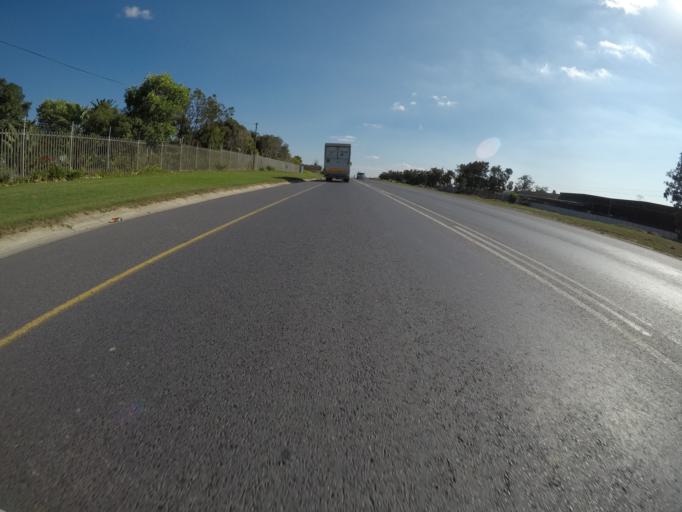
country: ZA
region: Western Cape
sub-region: City of Cape Town
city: Kraaifontein
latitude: -33.8856
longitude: 18.7487
